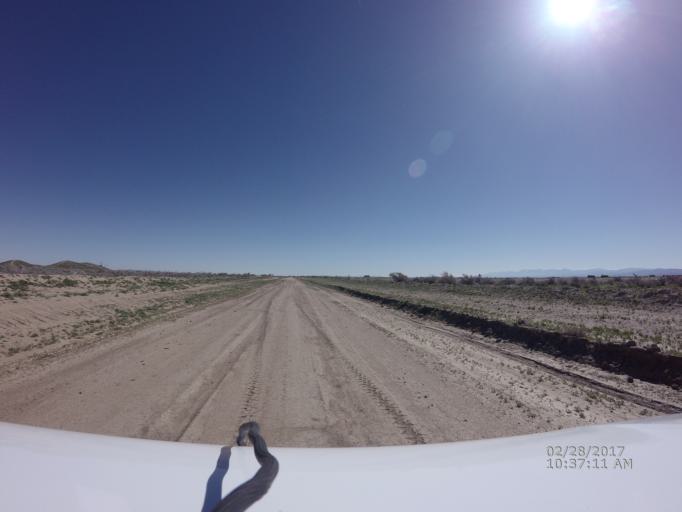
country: US
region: California
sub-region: Kern County
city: Rosamond
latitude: 34.7908
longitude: -118.3143
